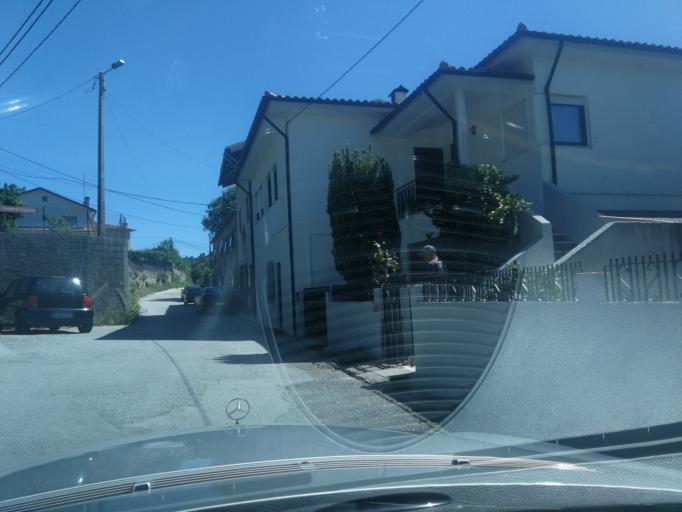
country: PT
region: Braga
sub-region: Braga
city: Adaufe
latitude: 41.5692
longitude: -8.4072
